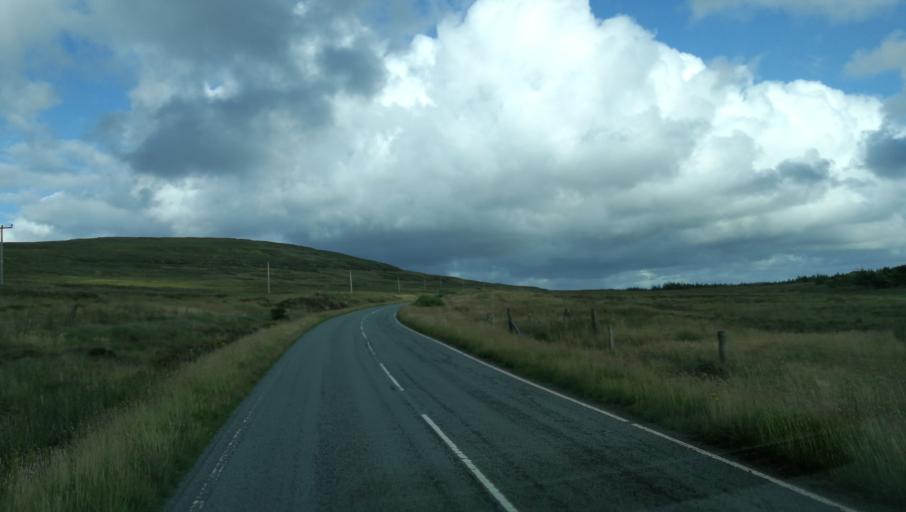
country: GB
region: Scotland
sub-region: Highland
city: Isle of Skye
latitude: 57.4692
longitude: -6.5280
